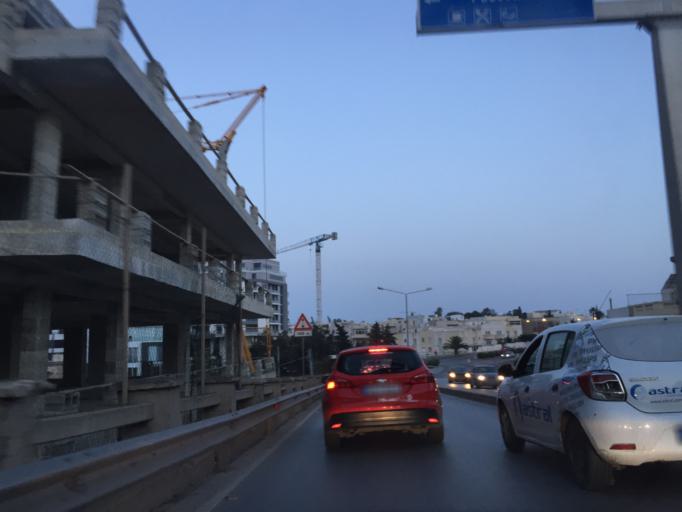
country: MT
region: Is-Swieqi
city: Swieqi
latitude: 35.9233
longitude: 14.4858
